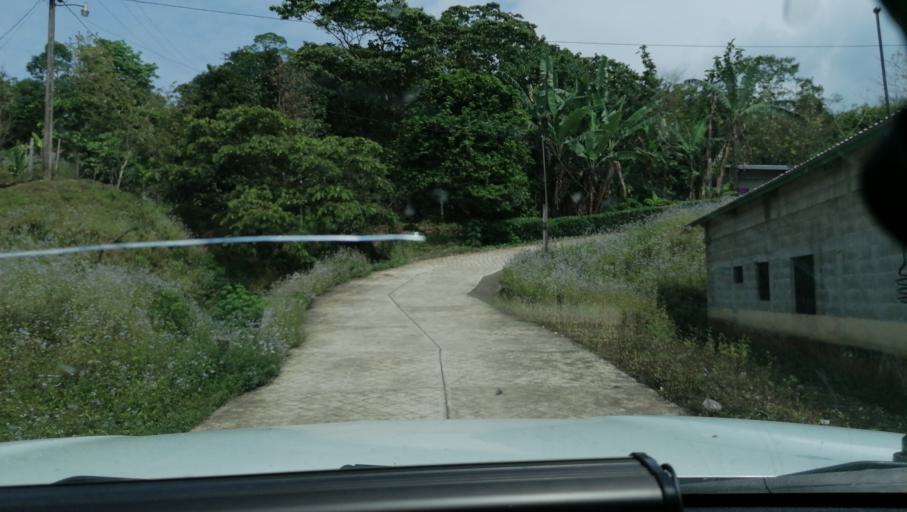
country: MX
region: Chiapas
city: Ocotepec
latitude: 17.3079
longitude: -93.1819
